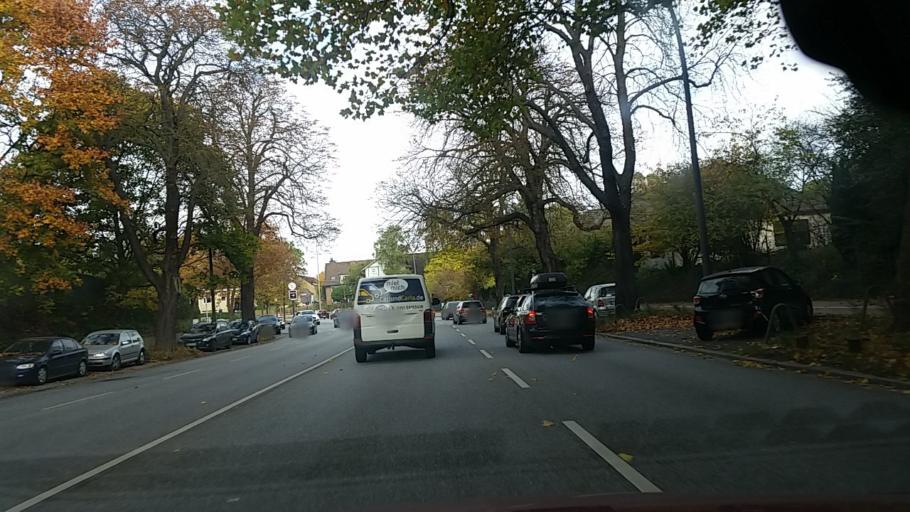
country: DE
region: Hamburg
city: Ohlsdorf
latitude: 53.6247
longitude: 10.0323
